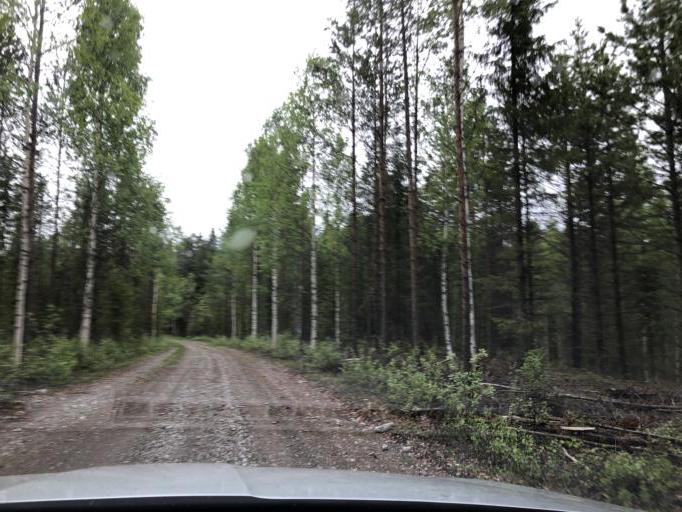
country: SE
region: Norrbotten
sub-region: Pitea Kommun
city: Roknas
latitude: 65.3976
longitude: 21.2648
